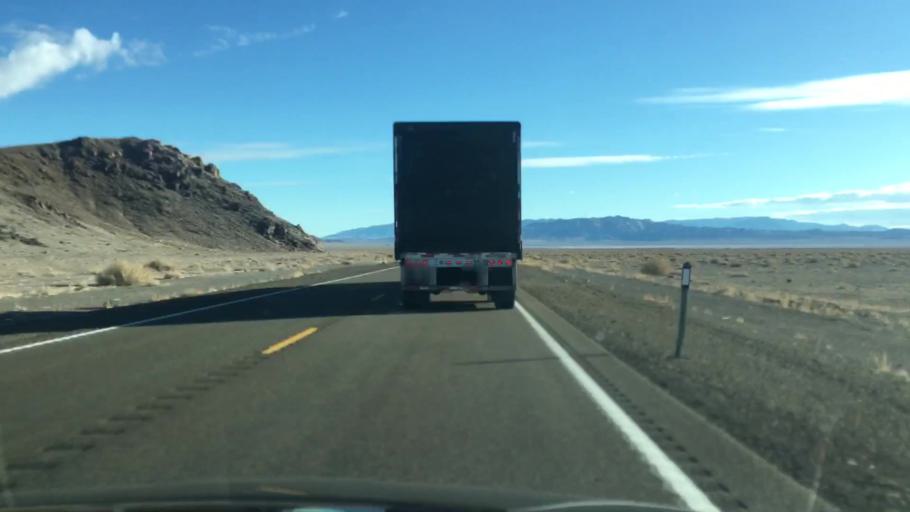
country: US
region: Nevada
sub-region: Nye County
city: Tonopah
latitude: 38.1502
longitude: -117.9472
